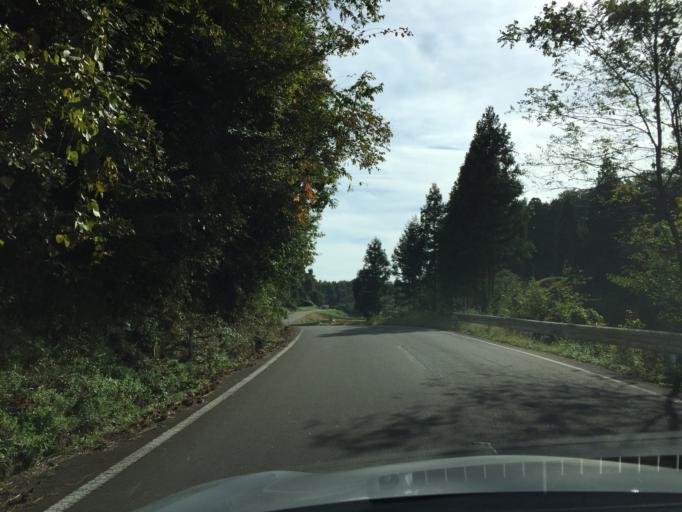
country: JP
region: Fukushima
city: Nihommatsu
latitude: 37.5749
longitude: 140.4978
